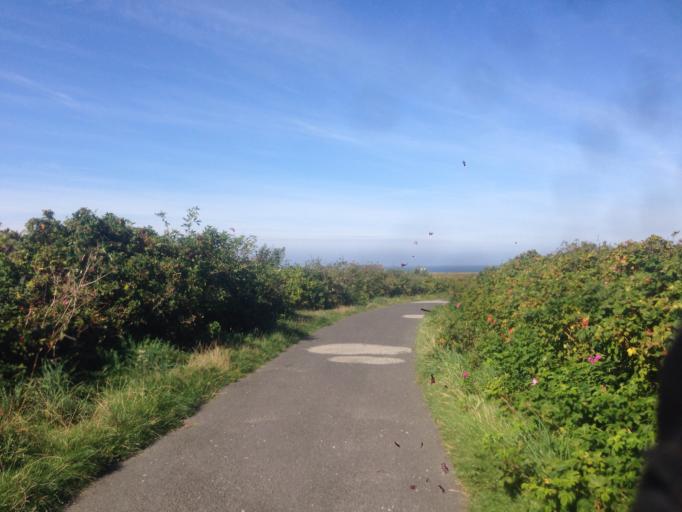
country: DE
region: Schleswig-Holstein
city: Tinnum
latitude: 54.9571
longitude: 8.3384
